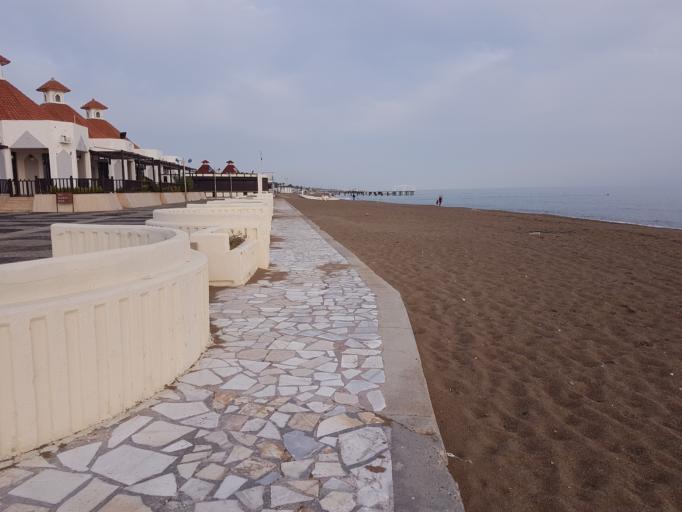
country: TR
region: Antalya
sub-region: Serik
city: Kumkoey
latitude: 36.8511
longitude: 30.8541
